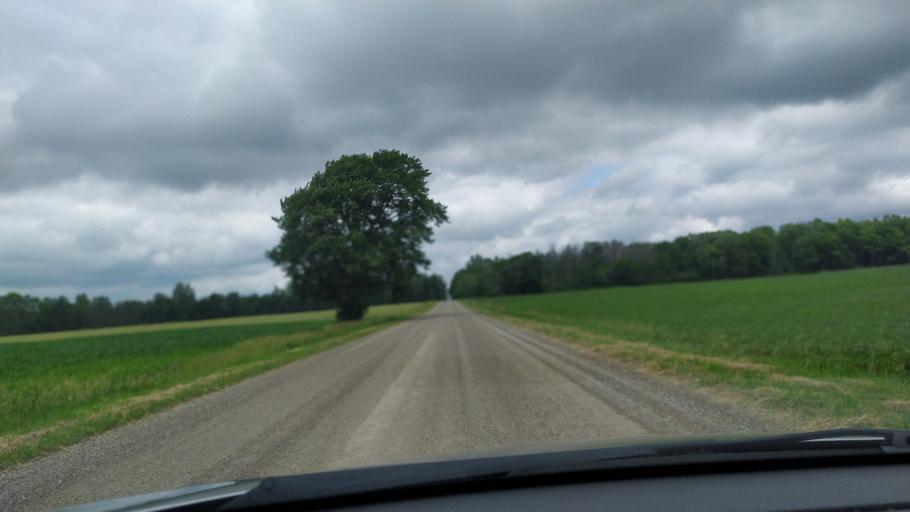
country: CA
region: Ontario
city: Stratford
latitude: 43.4130
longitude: -80.8881
